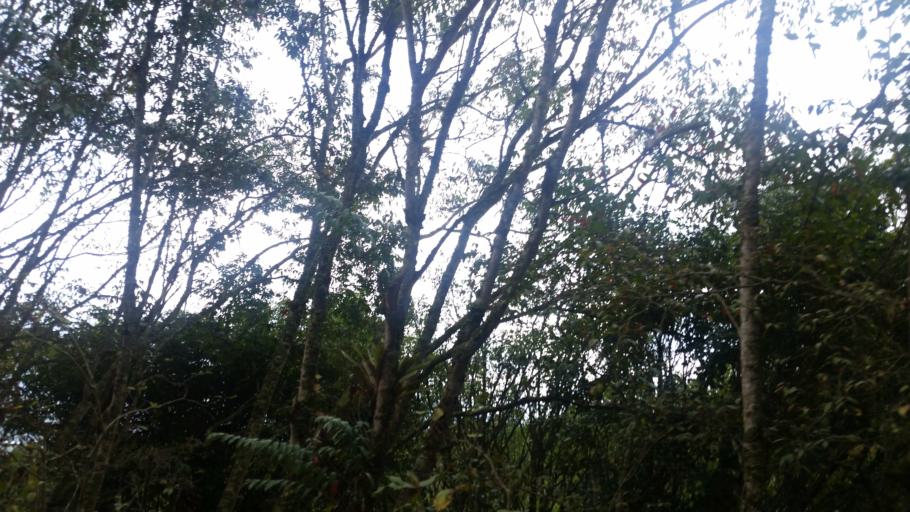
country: CO
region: Cundinamarca
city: Choachi
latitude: 4.5127
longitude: -73.9310
